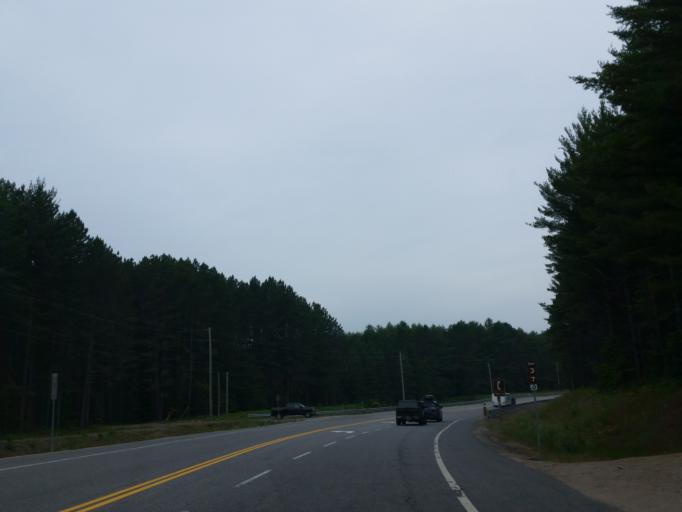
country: CA
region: Ontario
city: Bancroft
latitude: 45.5690
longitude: -78.4377
